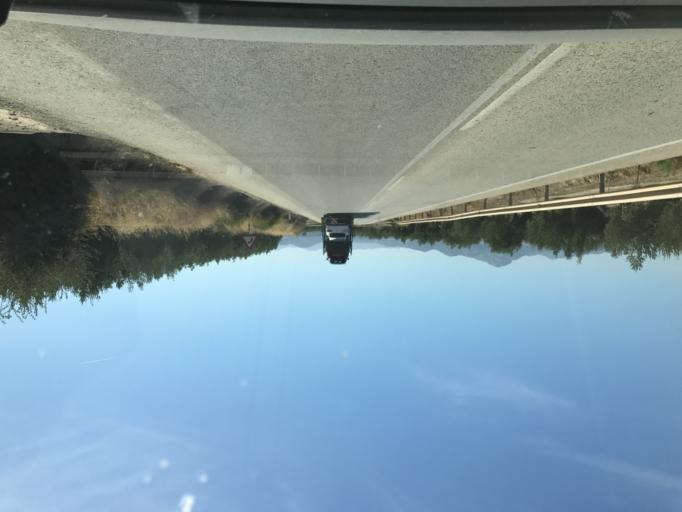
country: ES
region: Andalusia
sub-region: Province of Cordoba
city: Luque
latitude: 37.5645
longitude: -4.2191
